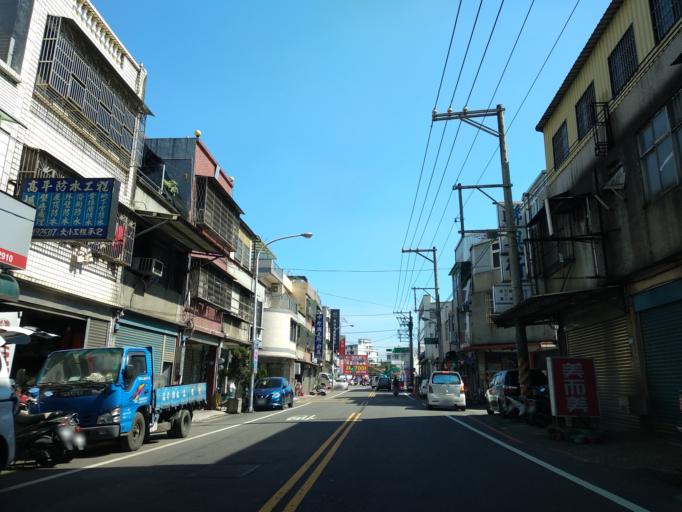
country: TW
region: Taiwan
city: Taoyuan City
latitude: 24.9474
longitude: 121.2094
